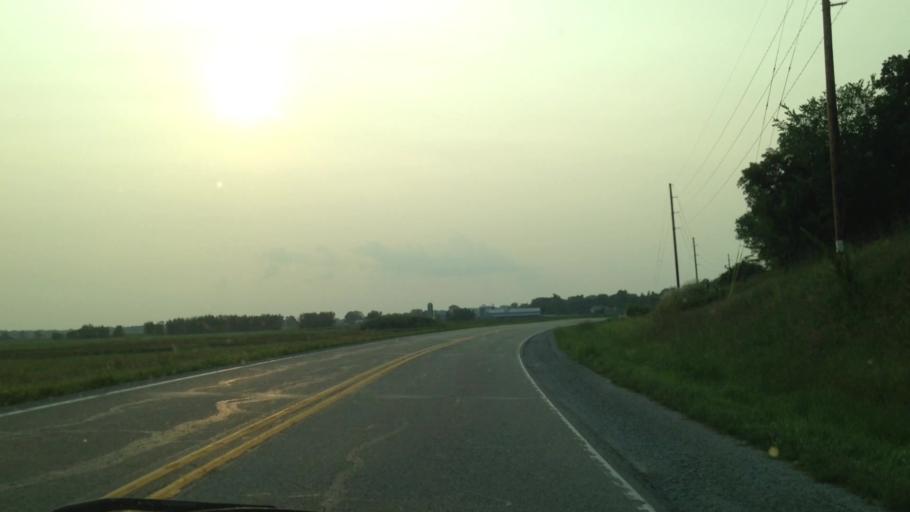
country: US
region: Iowa
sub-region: Benton County
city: Walford
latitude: 41.7985
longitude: -91.9289
